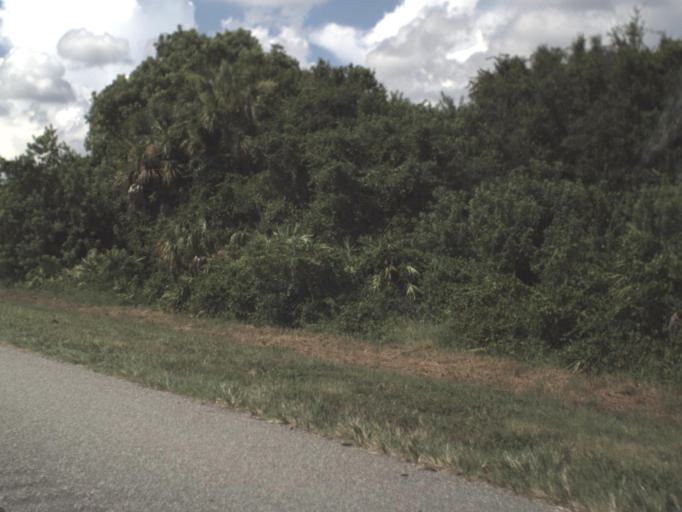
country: US
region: Florida
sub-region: Hillsborough County
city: Gibsonton
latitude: 27.8203
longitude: -82.3524
